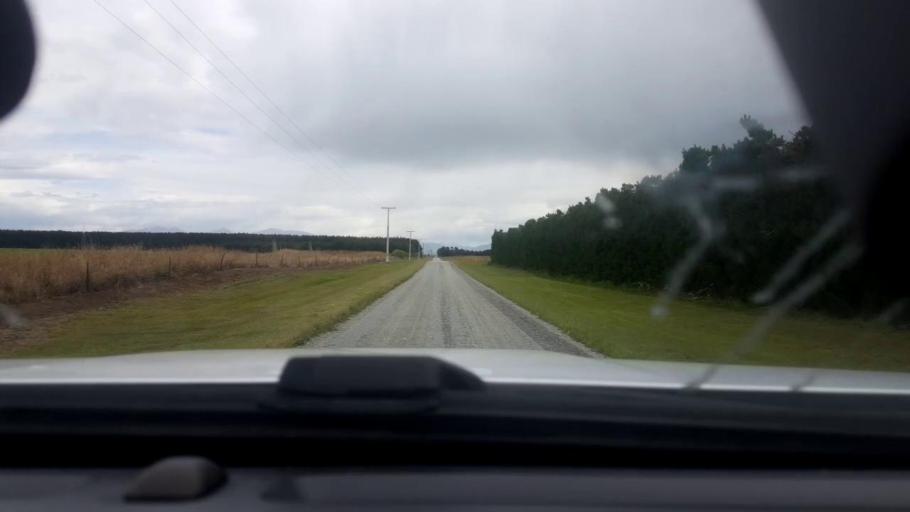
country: NZ
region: Canterbury
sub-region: Timaru District
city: Timaru
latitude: -44.1658
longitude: 171.4097
